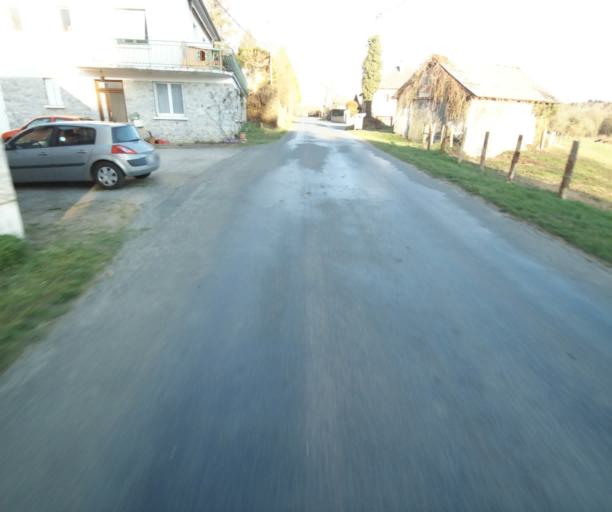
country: FR
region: Limousin
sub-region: Departement de la Correze
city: Saint-Clement
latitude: 45.3501
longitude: 1.6471
